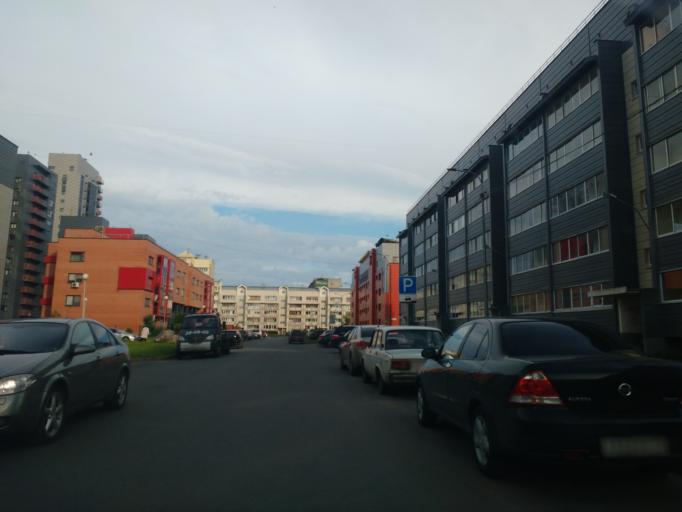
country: RU
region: Republic of Karelia
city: Petrozavodsk
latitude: 61.8066
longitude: 34.3362
